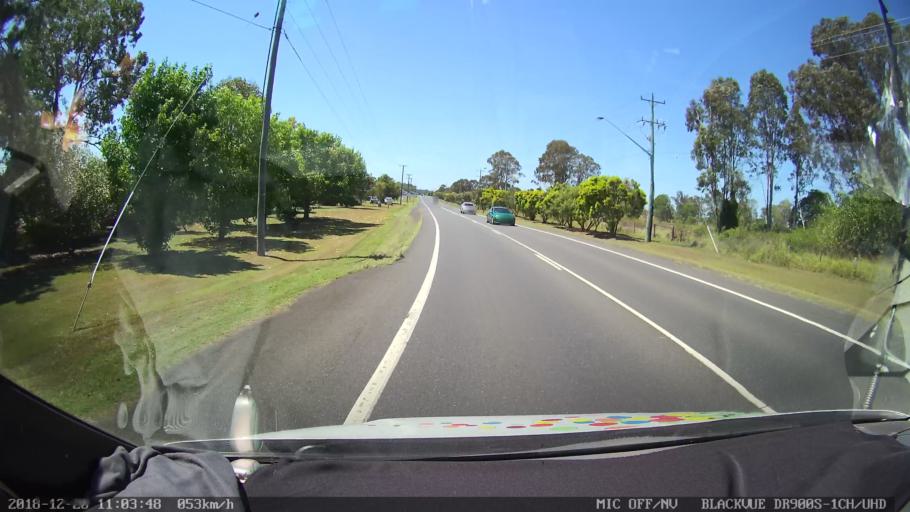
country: AU
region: New South Wales
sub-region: Richmond Valley
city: Casino
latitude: -28.8796
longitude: 153.0427
